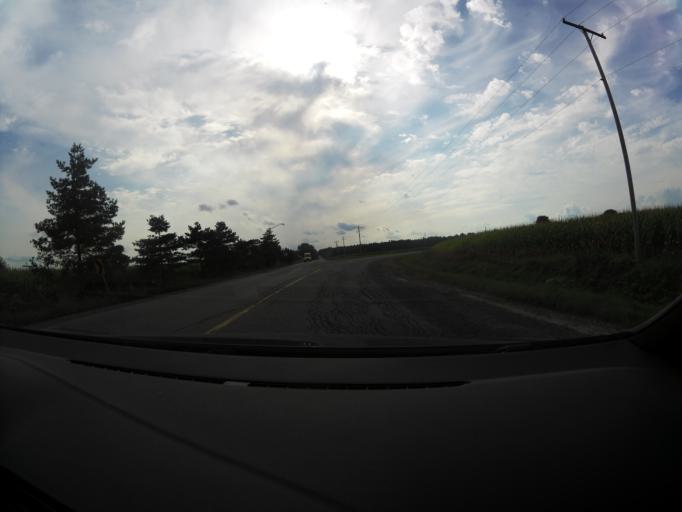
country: CA
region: Ontario
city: Carleton Place
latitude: 45.3510
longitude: -76.1317
